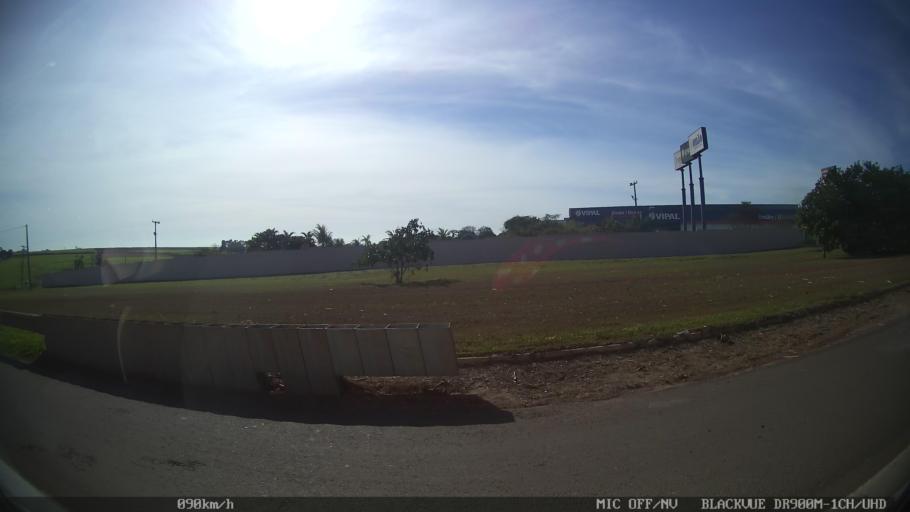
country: BR
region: Sao Paulo
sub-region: Rio Das Pedras
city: Rio das Pedras
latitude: -22.7902
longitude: -47.5828
